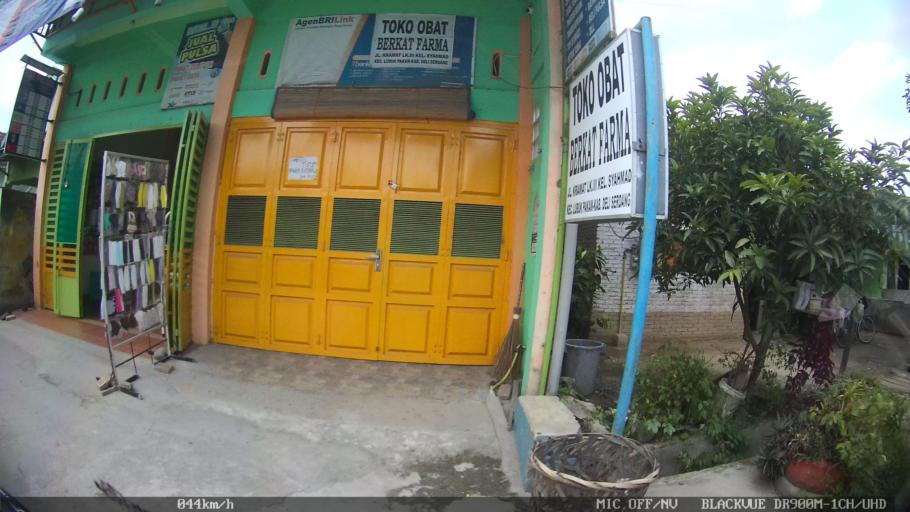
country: ID
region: North Sumatra
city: Percut
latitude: 3.5496
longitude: 98.8723
